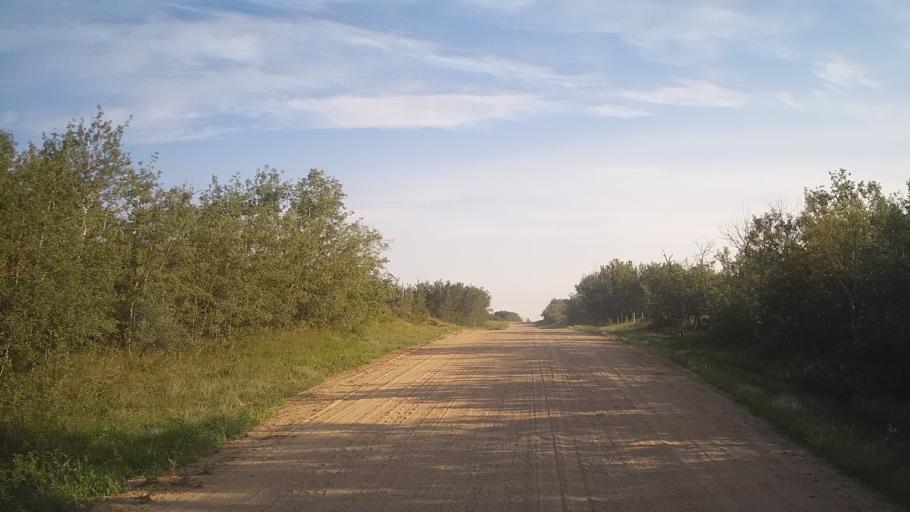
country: CA
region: Saskatchewan
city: Saskatoon
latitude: 51.8375
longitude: -106.5239
